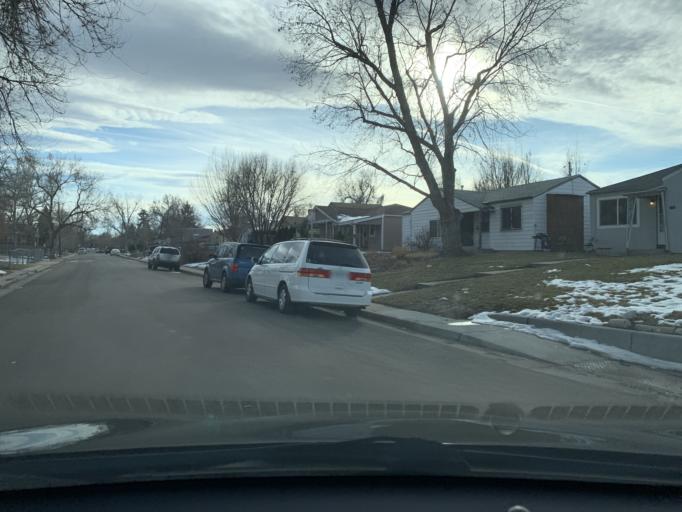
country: US
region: Colorado
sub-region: Jefferson County
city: Edgewater
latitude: 39.7348
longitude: -105.0287
